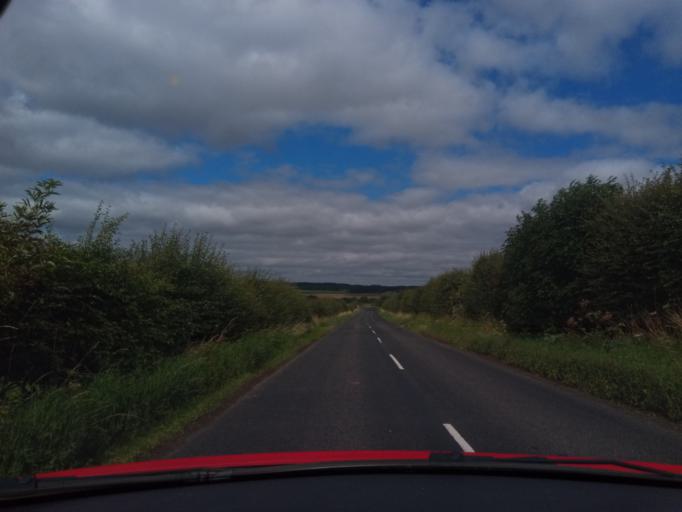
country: GB
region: Scotland
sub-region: The Scottish Borders
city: Kelso
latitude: 55.5382
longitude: -2.3663
